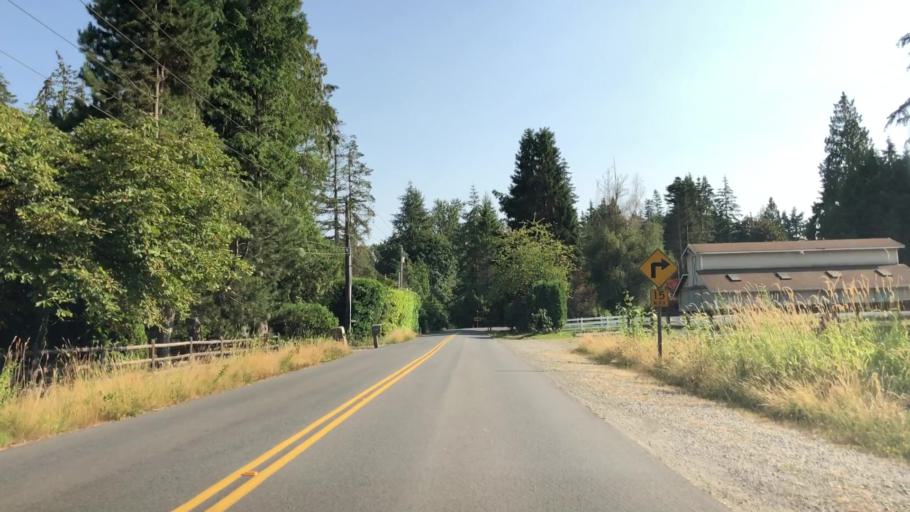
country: US
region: Washington
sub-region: King County
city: Woodinville
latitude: 47.7487
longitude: -122.1206
